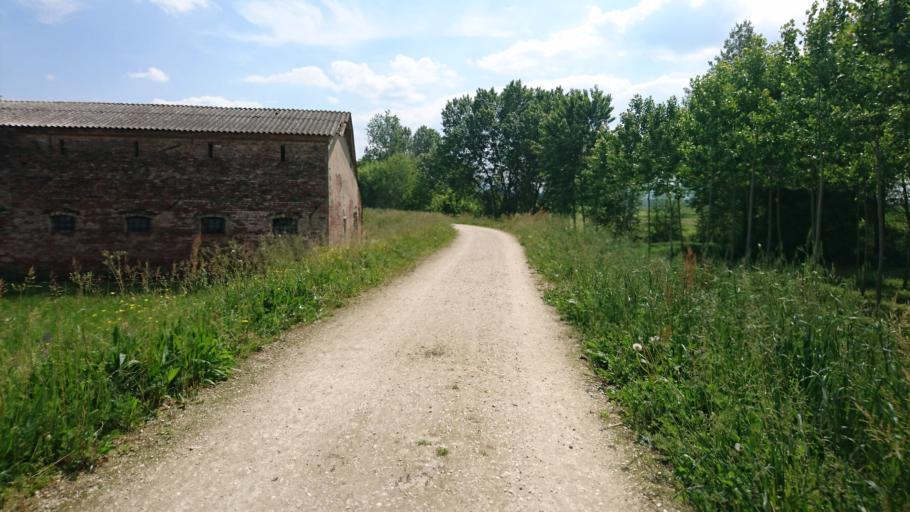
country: IT
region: Veneto
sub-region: Provincia di Padova
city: Veggiano
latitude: 45.4351
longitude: 11.7261
